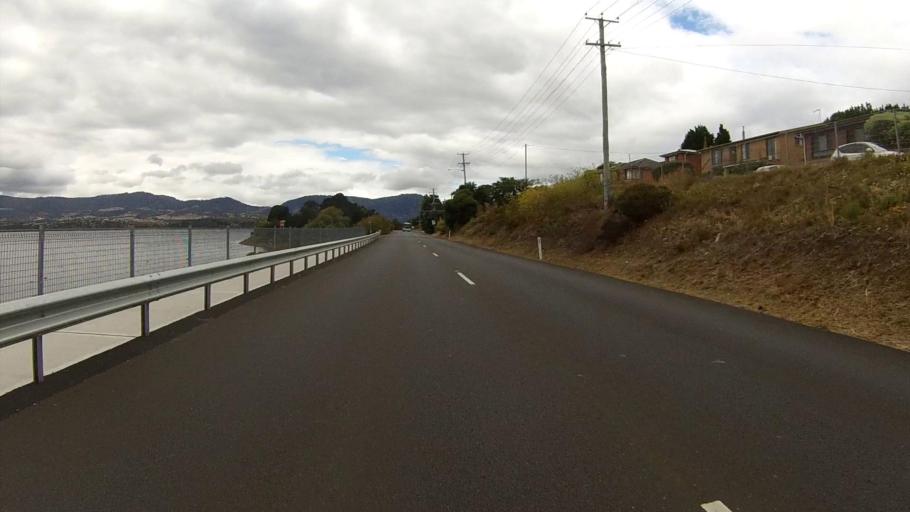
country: AU
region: Tasmania
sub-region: Glenorchy
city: Granton
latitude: -42.7597
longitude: 147.2371
